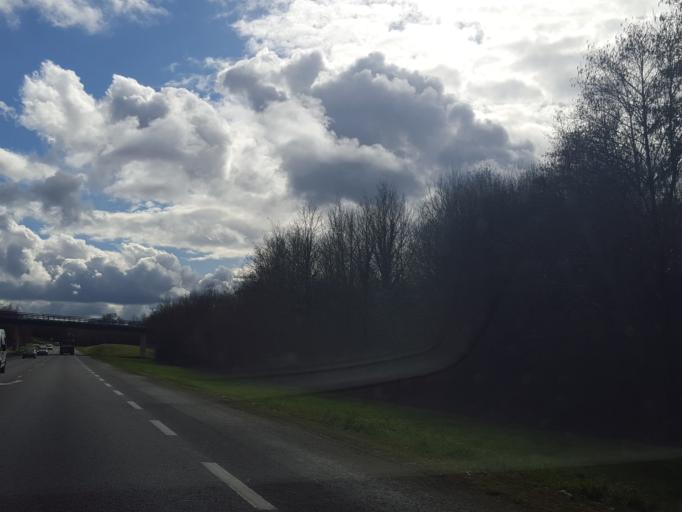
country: FR
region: Pays de la Loire
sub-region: Departement de la Vendee
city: La Roche-sur-Yon
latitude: 46.6857
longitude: -1.4116
